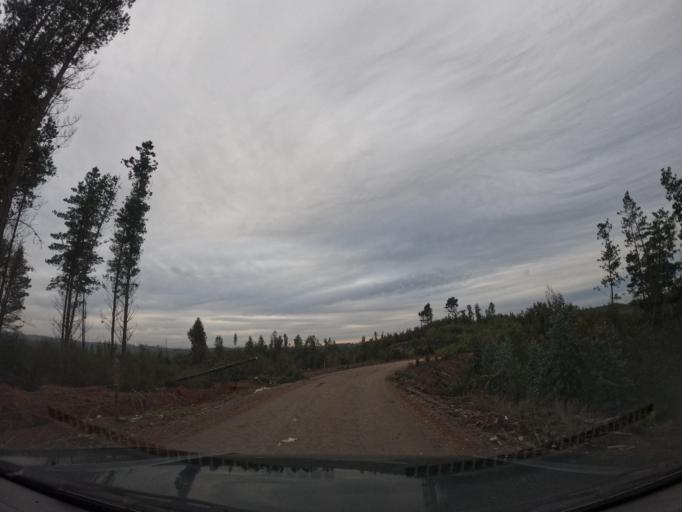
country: CL
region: Biobio
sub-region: Provincia de Concepcion
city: Chiguayante
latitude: -37.0107
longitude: -72.8863
